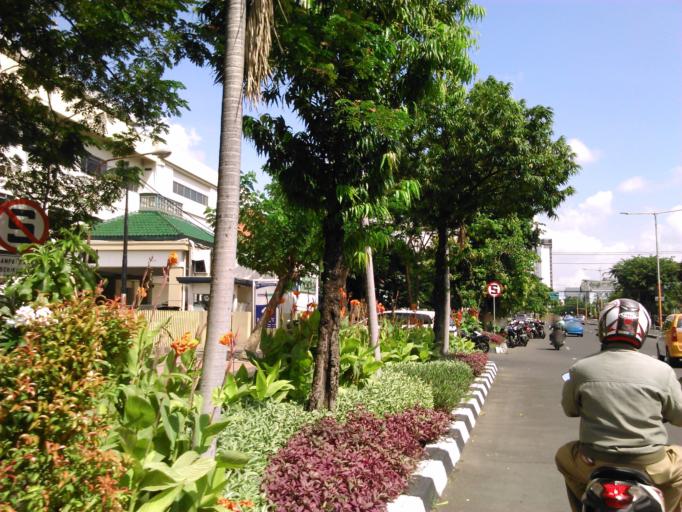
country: ID
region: East Java
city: Gubengairlangga
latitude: -7.2738
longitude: 112.7468
